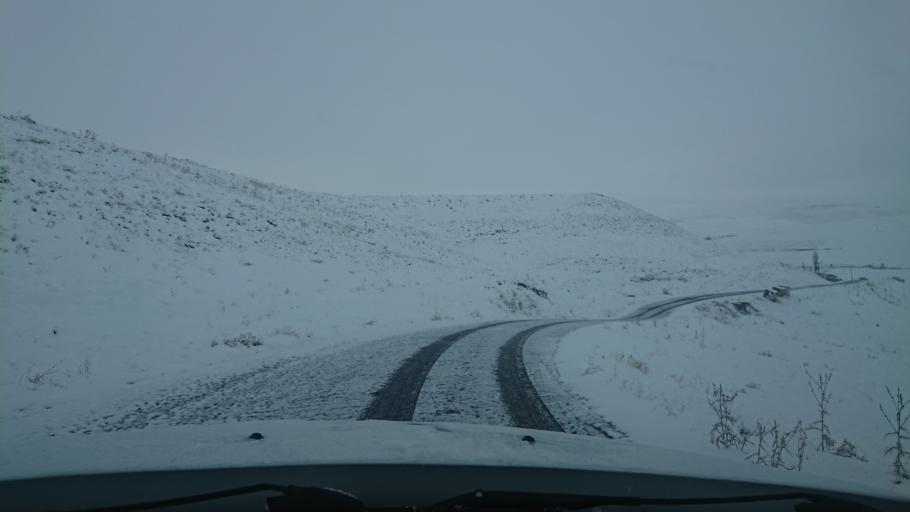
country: TR
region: Aksaray
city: Acipinar
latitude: 38.6730
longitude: 33.8632
